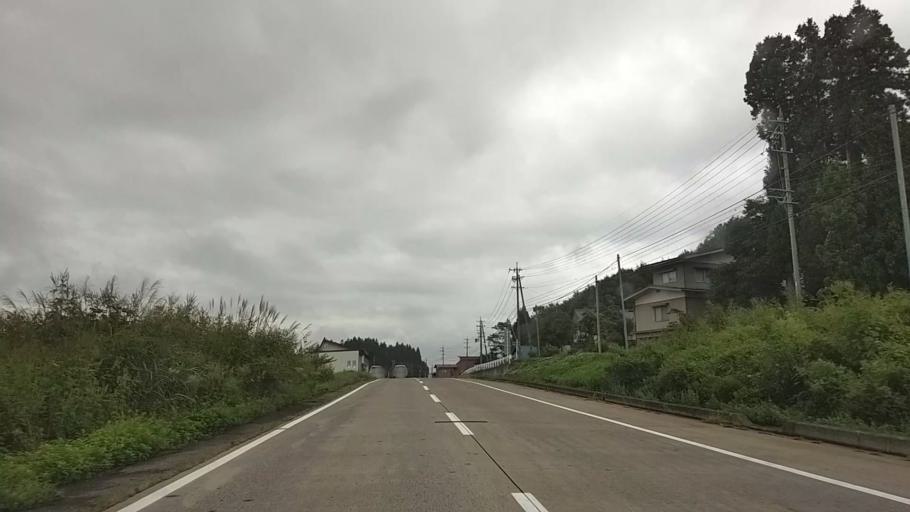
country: JP
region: Nagano
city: Iiyama
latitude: 36.8052
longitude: 138.3294
